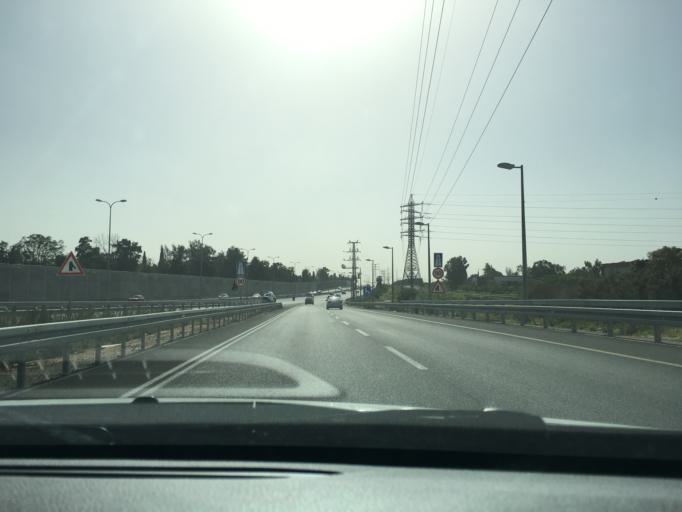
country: IL
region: Central District
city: Hod HaSharon
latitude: 32.1705
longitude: 34.8833
